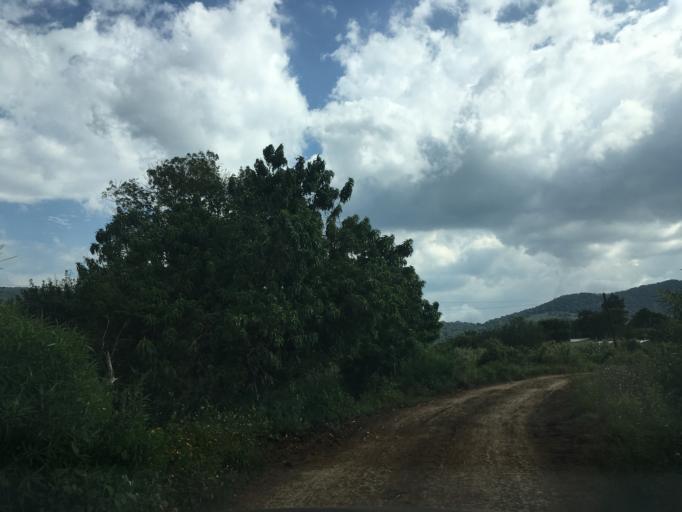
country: MX
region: Mexico
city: El Guayabito
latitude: 19.9005
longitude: -102.4999
